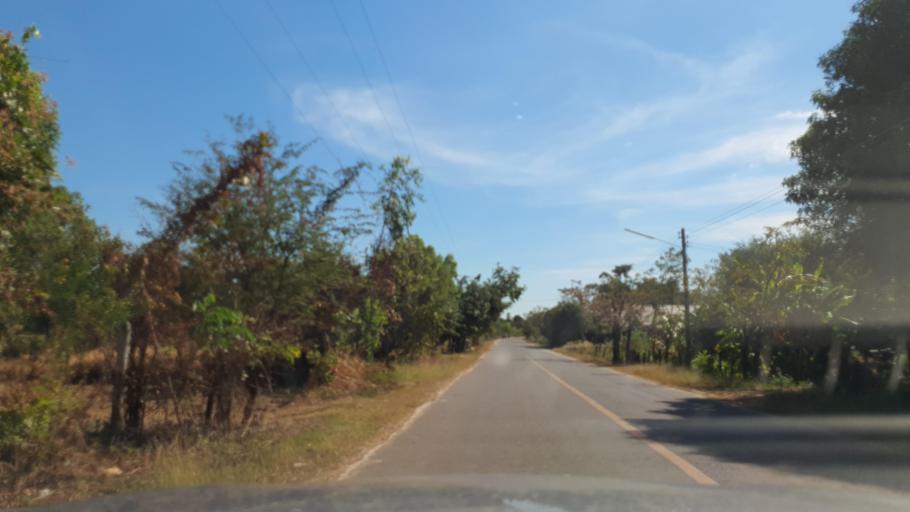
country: TH
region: Kalasin
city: Khao Wong
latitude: 16.7137
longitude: 104.1145
